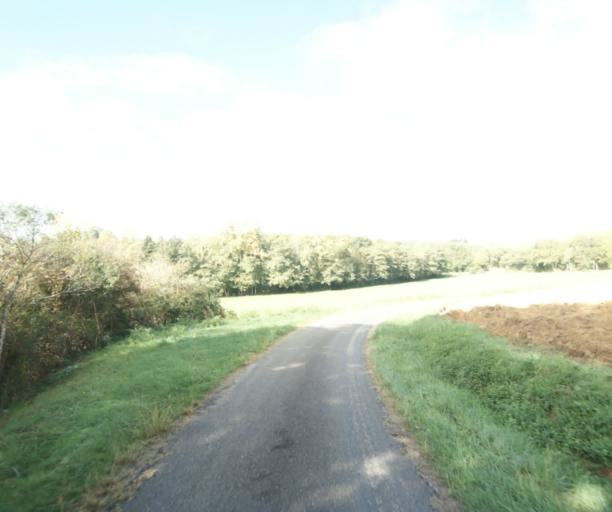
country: FR
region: Midi-Pyrenees
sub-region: Departement du Gers
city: Cazaubon
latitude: 43.8578
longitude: -0.0955
